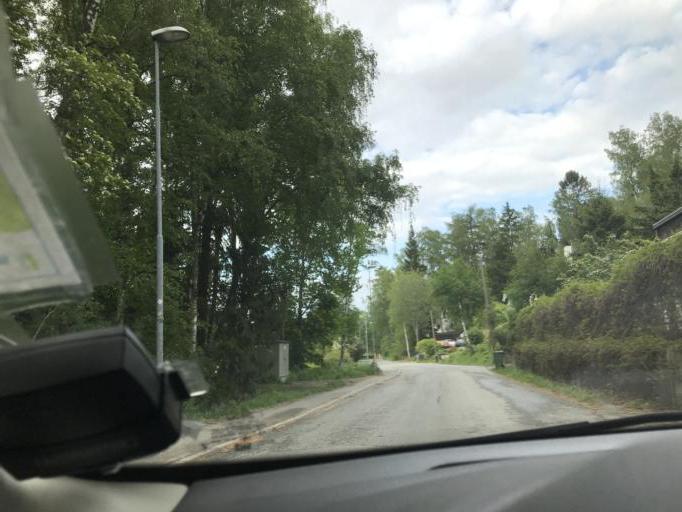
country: SE
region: Stockholm
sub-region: Botkyrka Kommun
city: Varsta
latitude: 59.1911
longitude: 17.7961
